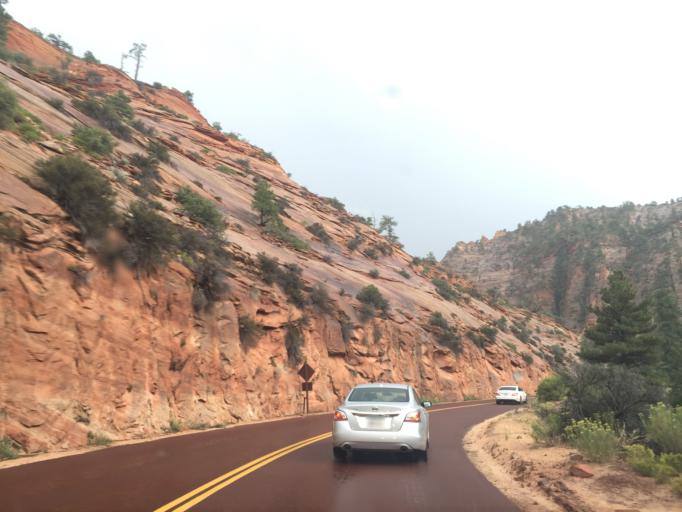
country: US
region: Utah
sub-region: Washington County
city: Hildale
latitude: 37.2182
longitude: -112.9214
